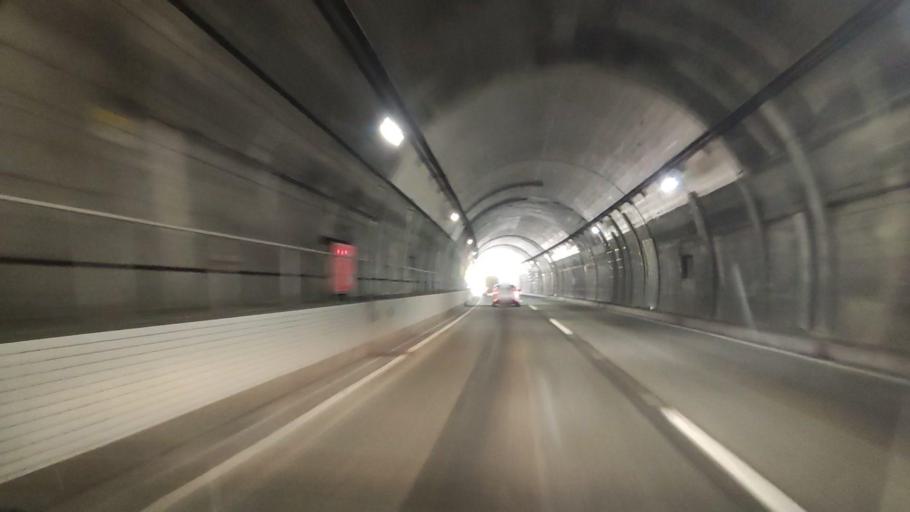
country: JP
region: Iwate
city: Ichinohe
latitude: 40.2368
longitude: 141.3974
